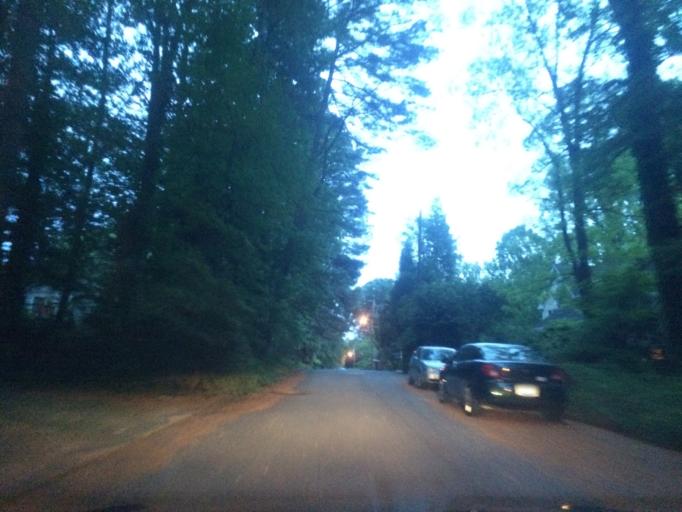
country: US
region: Georgia
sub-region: DeKalb County
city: Druid Hills
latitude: 33.8090
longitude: -84.3464
